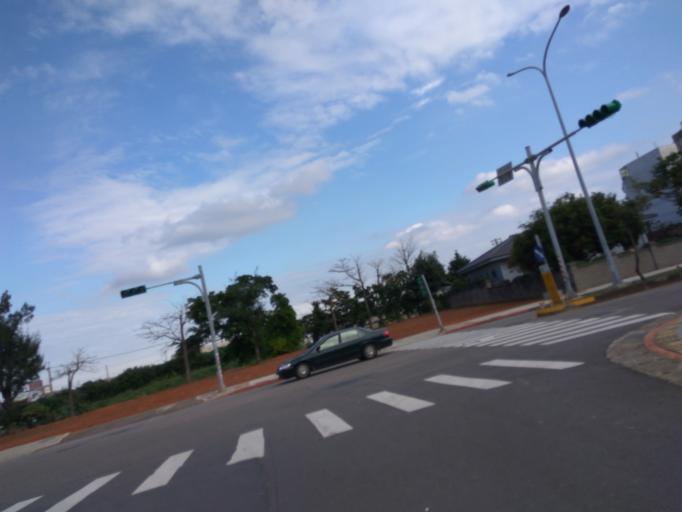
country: TW
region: Taiwan
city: Taoyuan City
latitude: 25.0614
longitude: 121.1779
